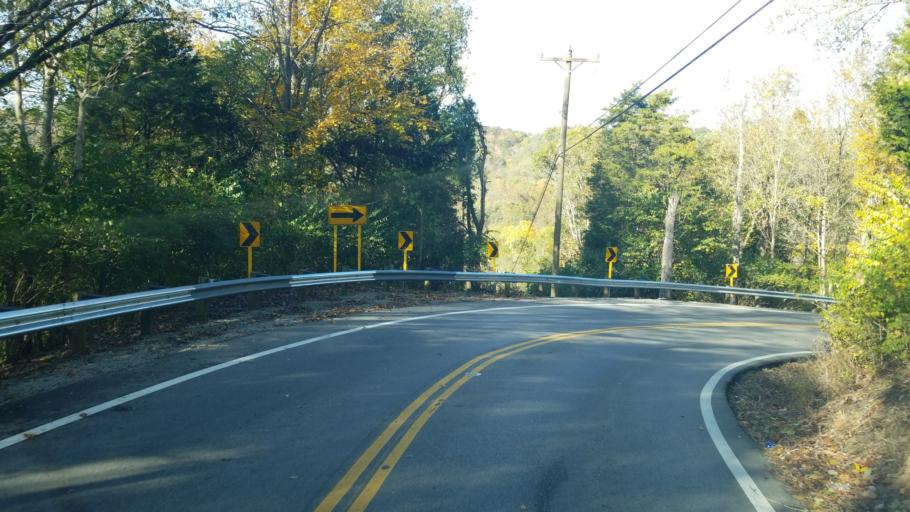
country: US
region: Ohio
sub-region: Warren County
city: Morrow
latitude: 39.4080
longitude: -84.0956
